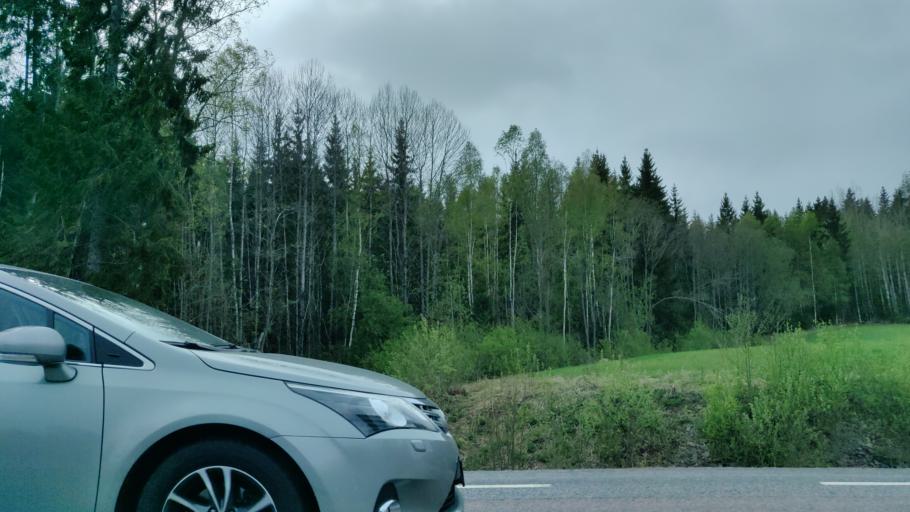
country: SE
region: Vaermland
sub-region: Forshaga Kommun
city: Deje
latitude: 59.6575
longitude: 13.4385
